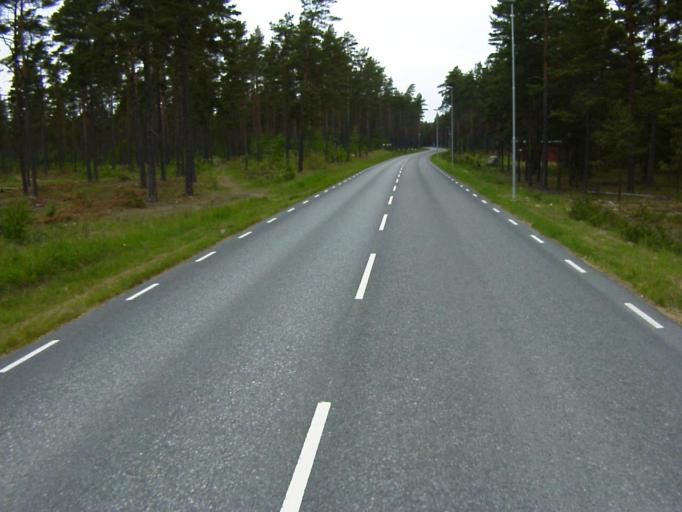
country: SE
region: Skane
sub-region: Kristianstads Kommun
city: Ahus
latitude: 55.9457
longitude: 14.3008
